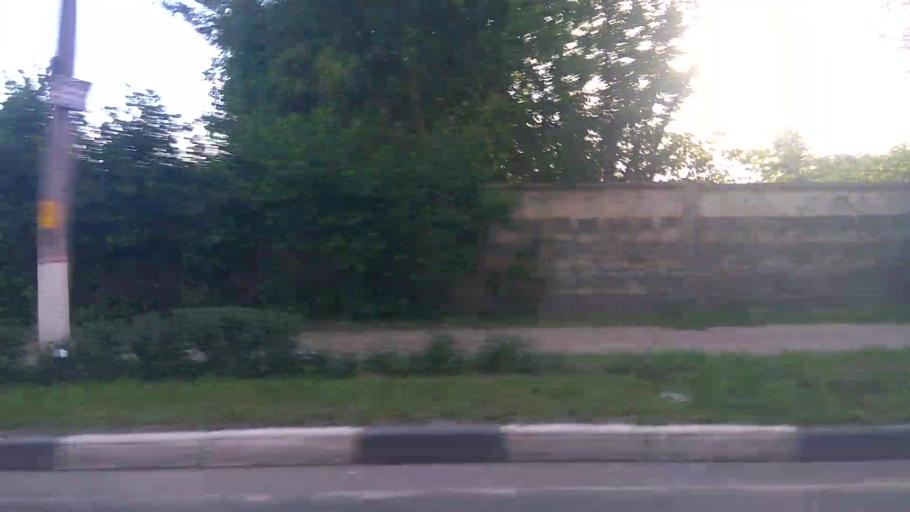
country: RU
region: Moskovskaya
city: Korolev
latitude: 55.9209
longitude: 37.7835
